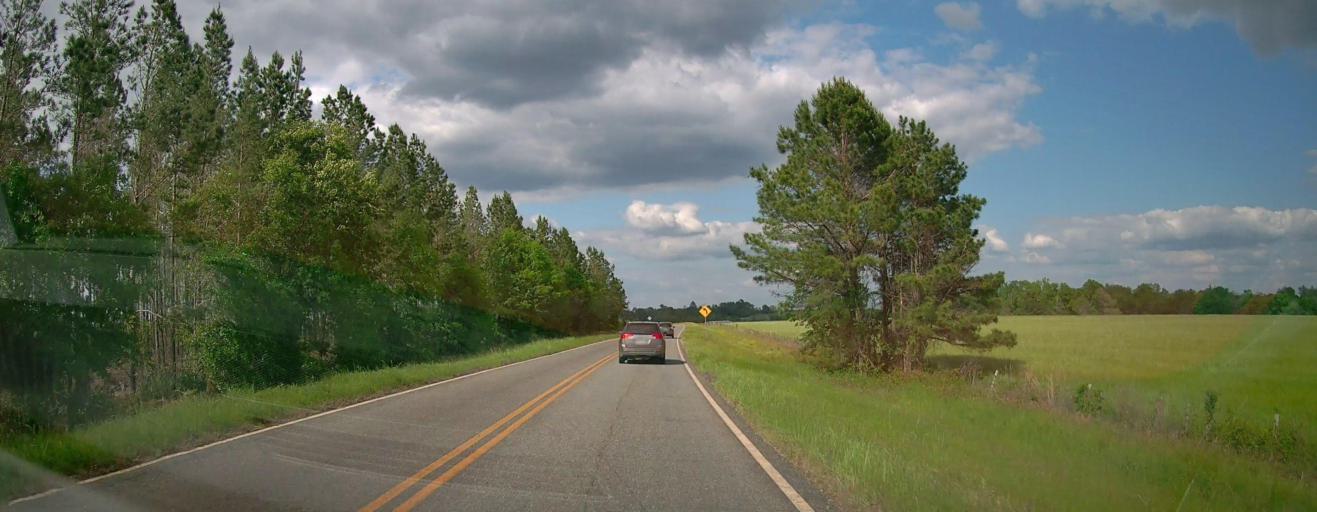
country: US
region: Georgia
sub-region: Laurens County
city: East Dublin
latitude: 32.7252
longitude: -82.9124
